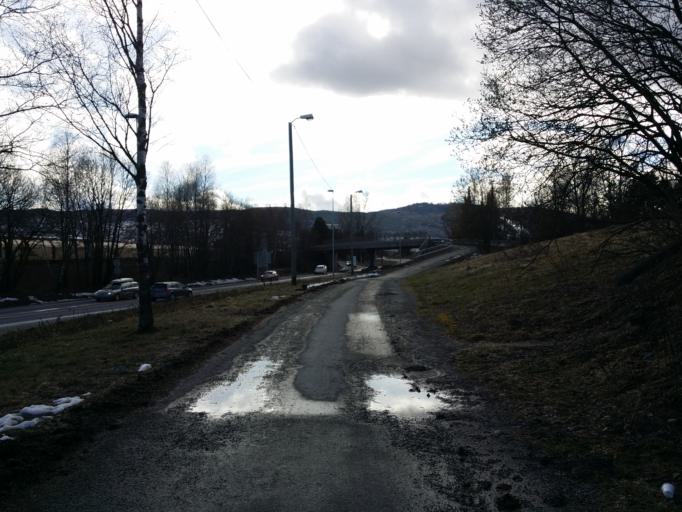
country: NO
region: Buskerud
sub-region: Drammen
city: Drammen
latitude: 59.7466
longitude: 10.2377
